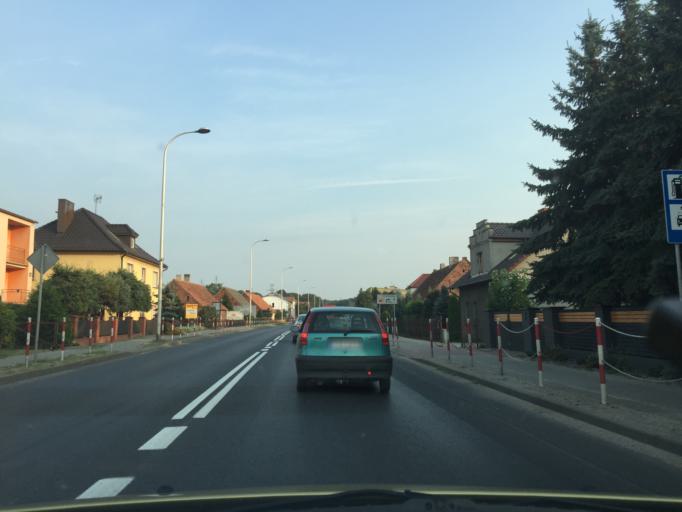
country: PL
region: Greater Poland Voivodeship
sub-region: Powiat jarocinski
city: Jarocin
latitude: 51.9600
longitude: 17.5148
